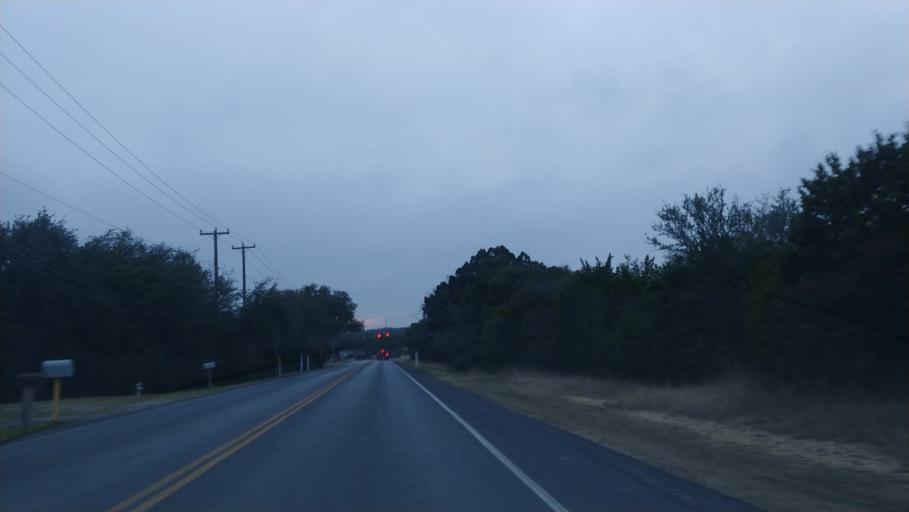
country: US
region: Texas
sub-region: Bexar County
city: Helotes
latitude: 29.5825
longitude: -98.6901
